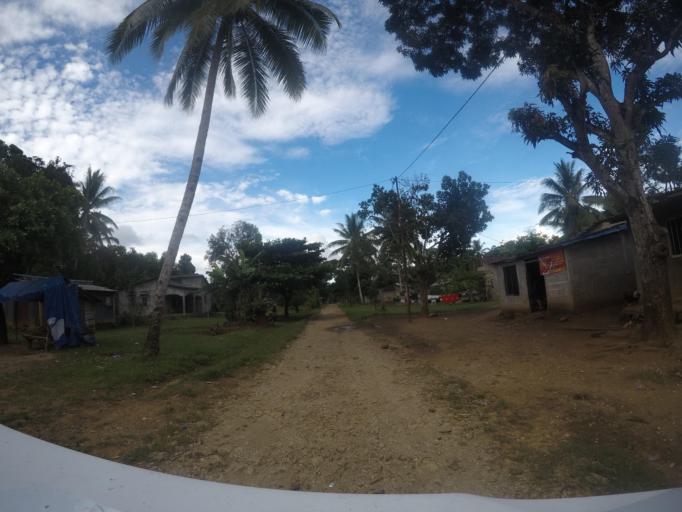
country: TL
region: Lautem
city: Lospalos
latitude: -8.5023
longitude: 126.9938
